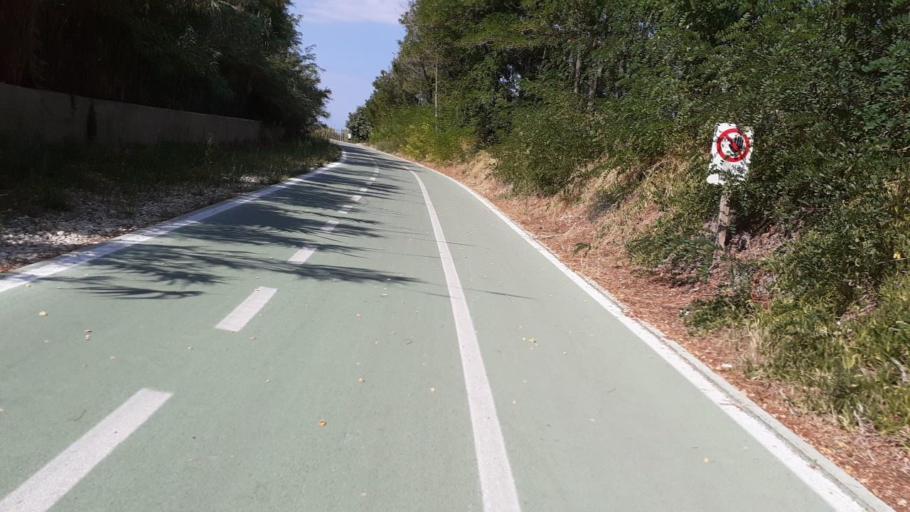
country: IT
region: Abruzzo
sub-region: Provincia di Chieti
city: Fossacesia
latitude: 42.2690
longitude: 14.5025
